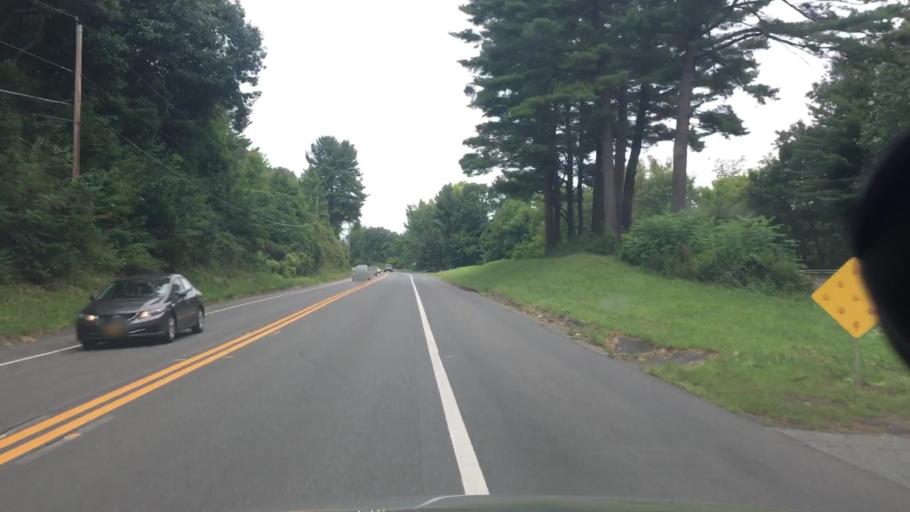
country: US
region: Massachusetts
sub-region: Franklin County
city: Greenfield
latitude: 42.5909
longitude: -72.6314
